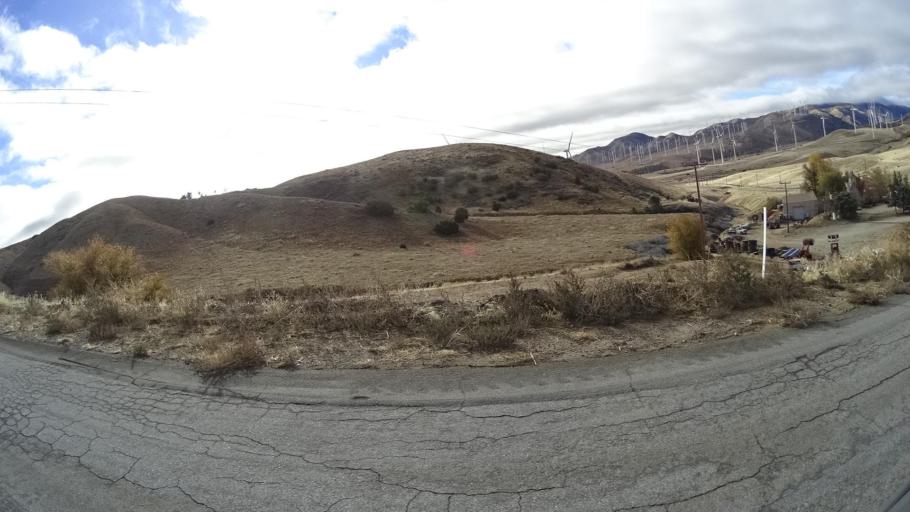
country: US
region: California
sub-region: Kern County
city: Tehachapi
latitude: 35.0676
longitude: -118.3511
